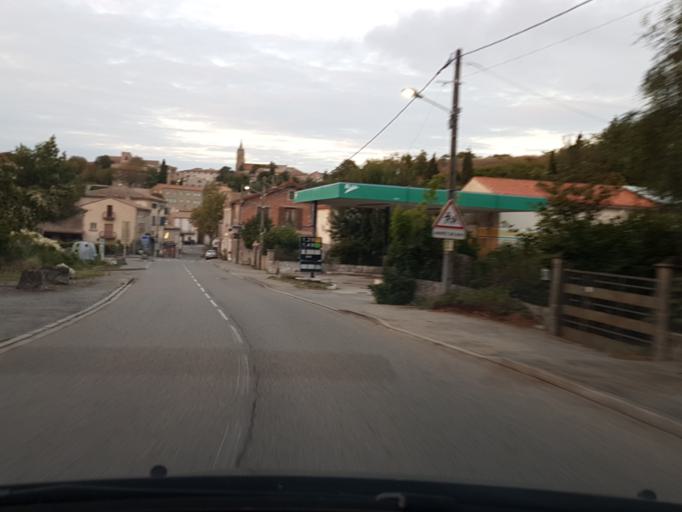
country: FR
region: Languedoc-Roussillon
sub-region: Departement de l'Aude
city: Bram
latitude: 43.1832
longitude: 2.0343
